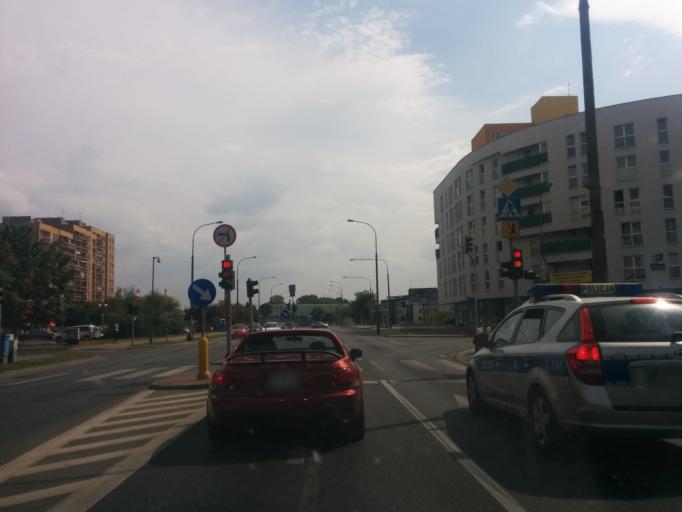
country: PL
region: Masovian Voivodeship
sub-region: Warszawa
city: Bialoleka
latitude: 52.3156
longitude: 20.9618
